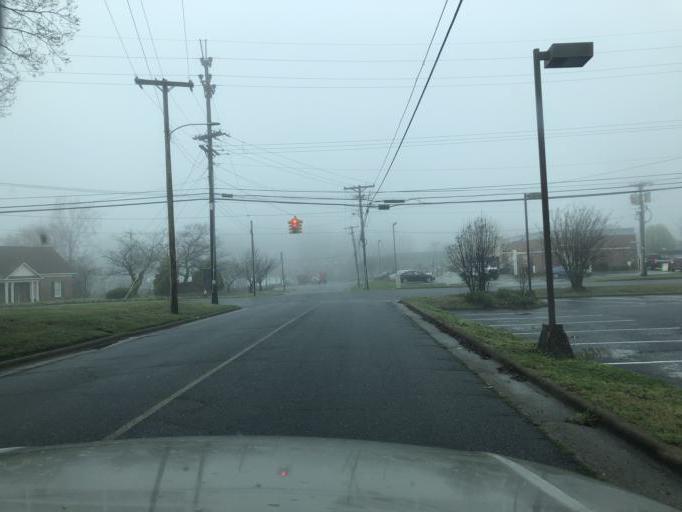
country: US
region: North Carolina
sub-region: Gaston County
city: Cherryville
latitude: 35.3849
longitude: -81.3687
